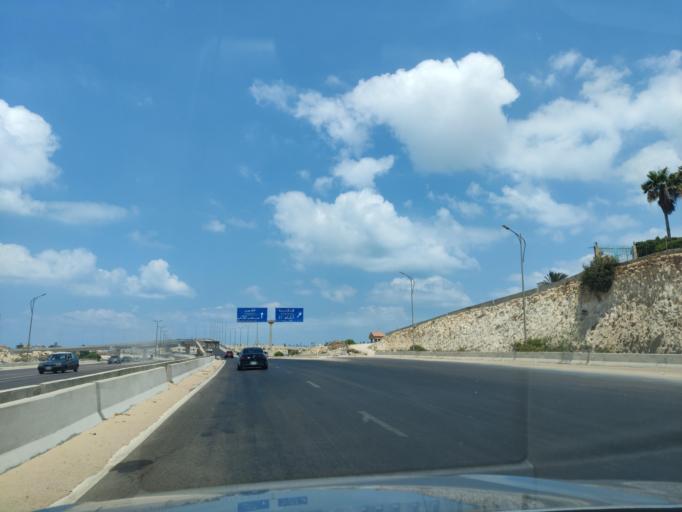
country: EG
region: Alexandria
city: Alexandria
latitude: 31.0110
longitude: 29.6359
